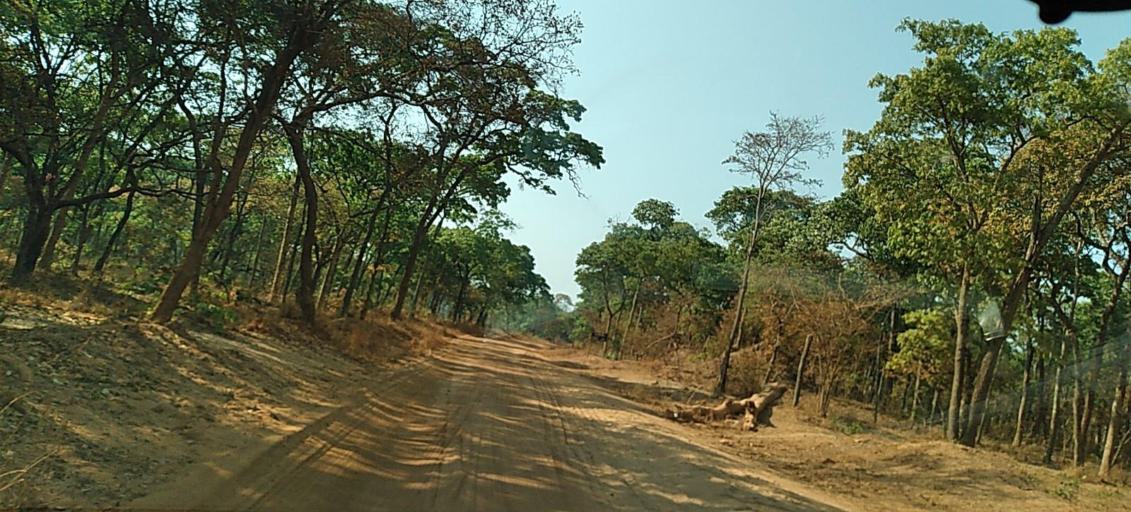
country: ZM
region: North-Western
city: Kasempa
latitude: -13.6561
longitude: 26.0081
